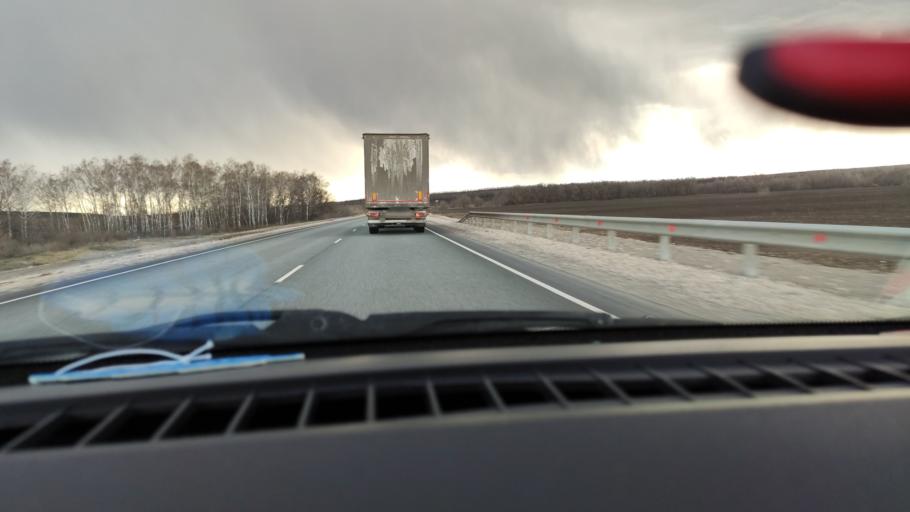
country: RU
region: Saratov
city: Yelshanka
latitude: 51.8521
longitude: 46.4895
